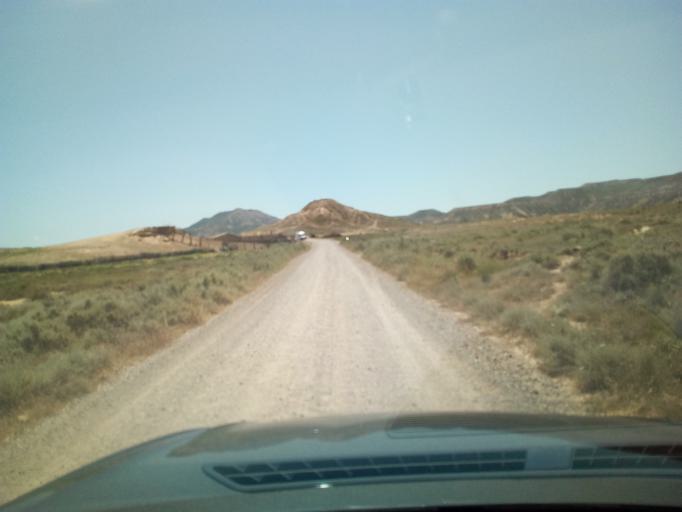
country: ES
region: Navarre
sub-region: Provincia de Navarra
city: Fustinana
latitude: 42.1667
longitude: -1.4400
